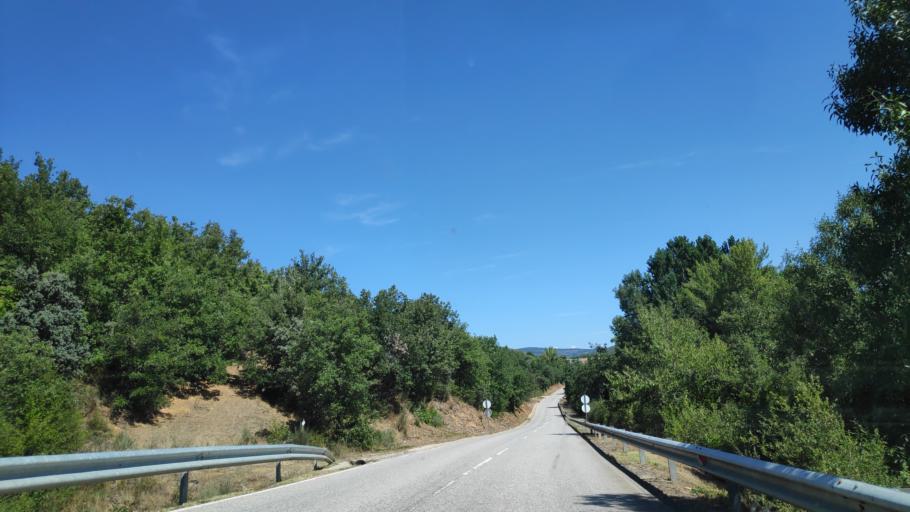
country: PT
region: Braganca
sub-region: Braganca Municipality
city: Braganca
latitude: 41.8484
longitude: -6.7474
